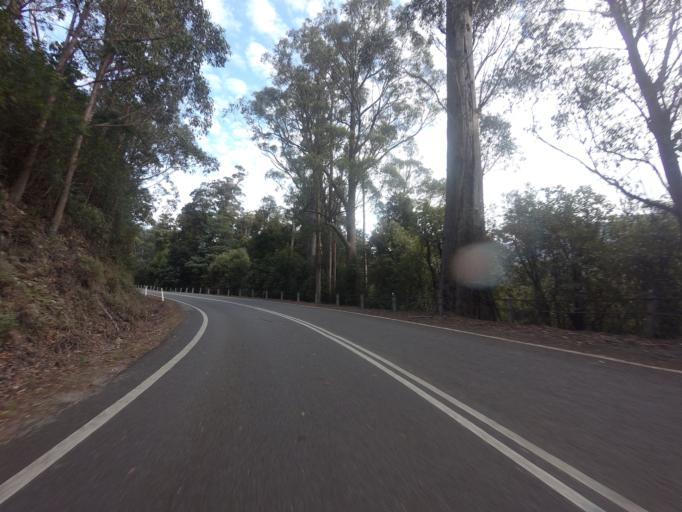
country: AU
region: Tasmania
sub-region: Meander Valley
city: Deloraine
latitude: -41.6549
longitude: 146.7224
